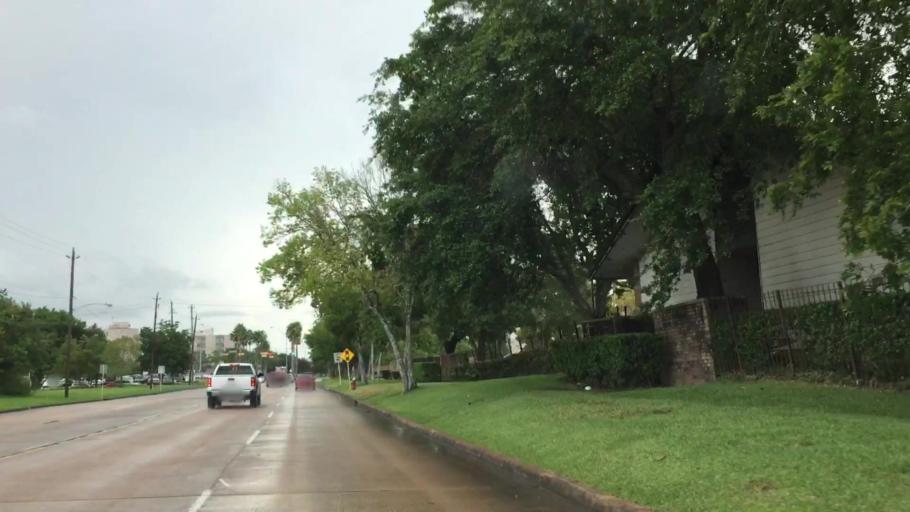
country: US
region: Texas
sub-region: Harris County
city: Webster
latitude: 29.5378
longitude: -95.1309
